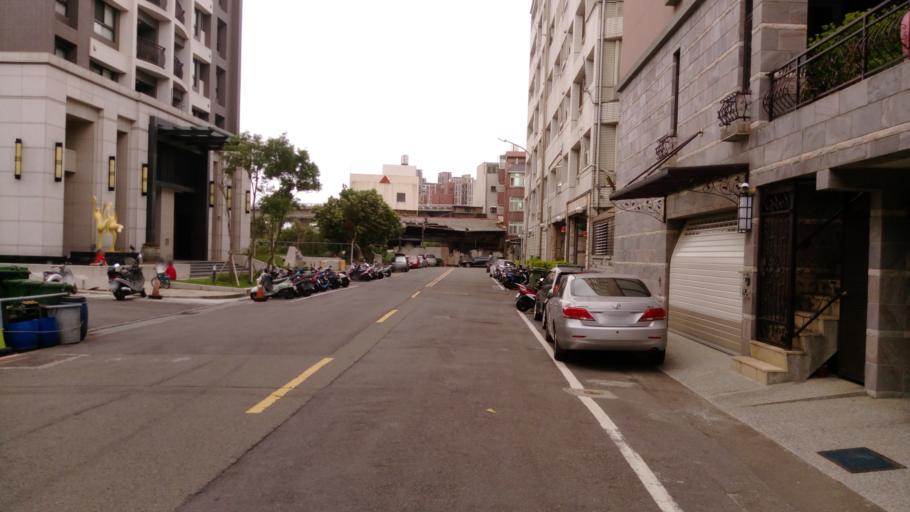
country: TW
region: Taiwan
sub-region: Hsinchu
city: Hsinchu
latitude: 24.7942
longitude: 120.9501
